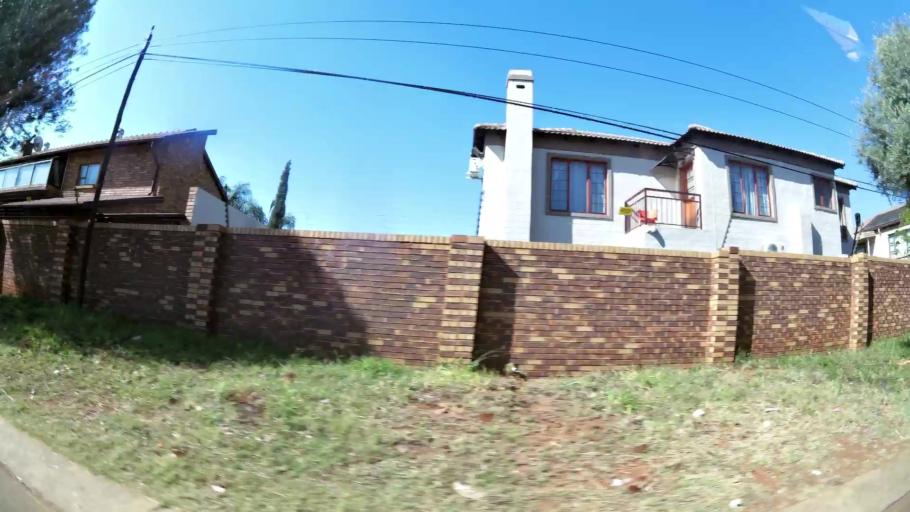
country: ZA
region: Gauteng
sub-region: City of Tshwane Metropolitan Municipality
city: Pretoria
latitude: -25.6596
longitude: 28.2504
